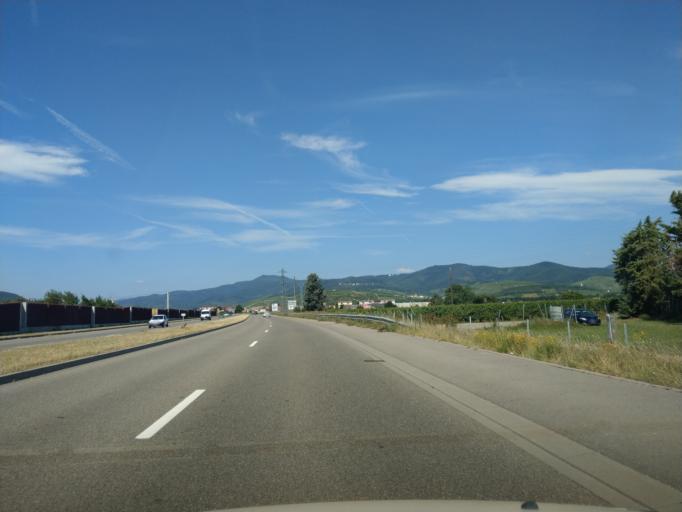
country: FR
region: Alsace
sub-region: Departement du Haut-Rhin
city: Ingersheim
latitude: 48.0922
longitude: 7.3260
